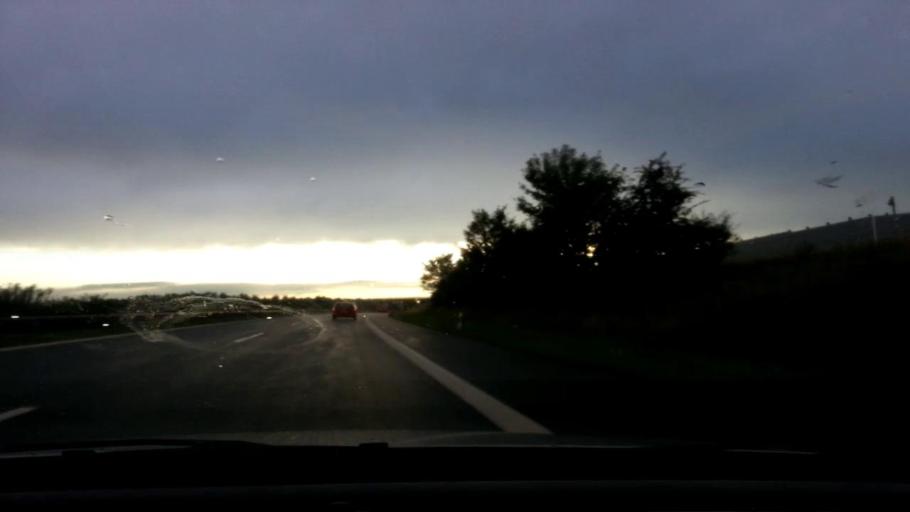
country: DE
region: Bavaria
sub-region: Upper Franconia
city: Wonsees
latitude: 50.0058
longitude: 11.2641
